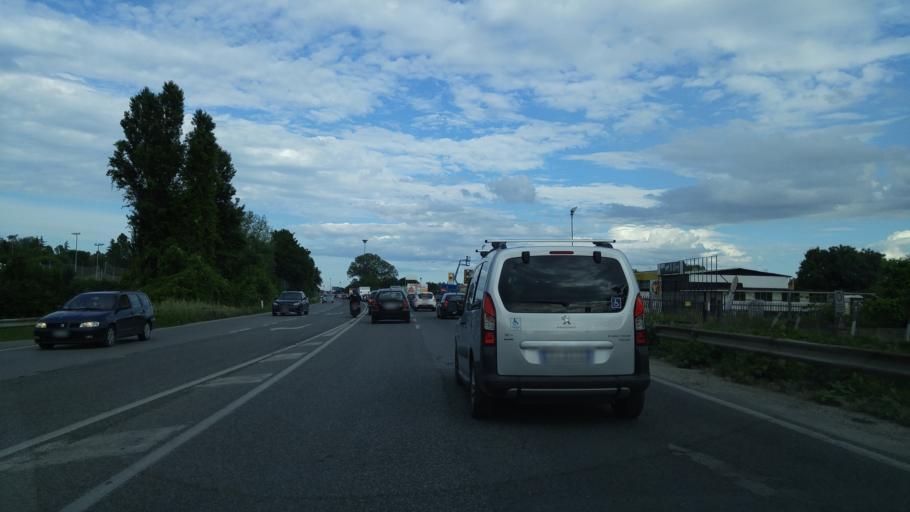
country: IT
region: Emilia-Romagna
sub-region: Provincia di Rimini
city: Rimini
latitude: 44.0424
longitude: 12.5664
